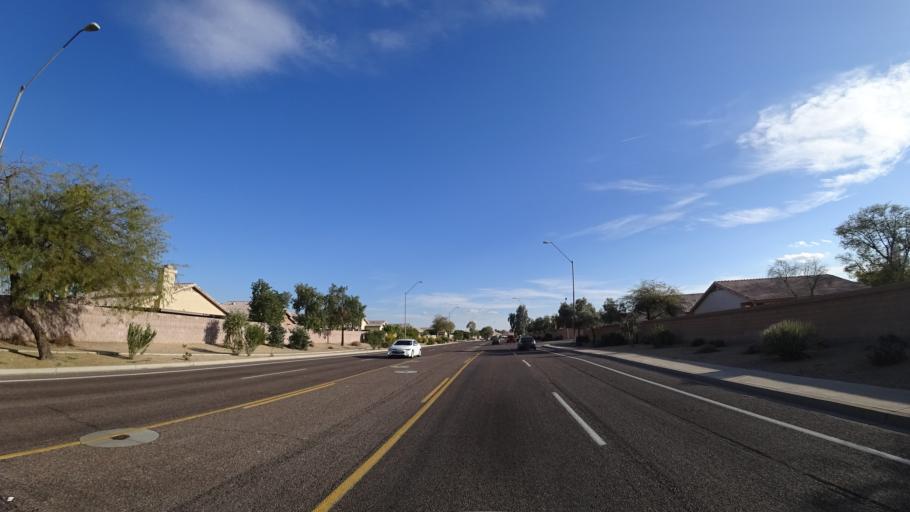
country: US
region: Arizona
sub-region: Maricopa County
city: Sun City
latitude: 33.6340
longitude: -112.2525
